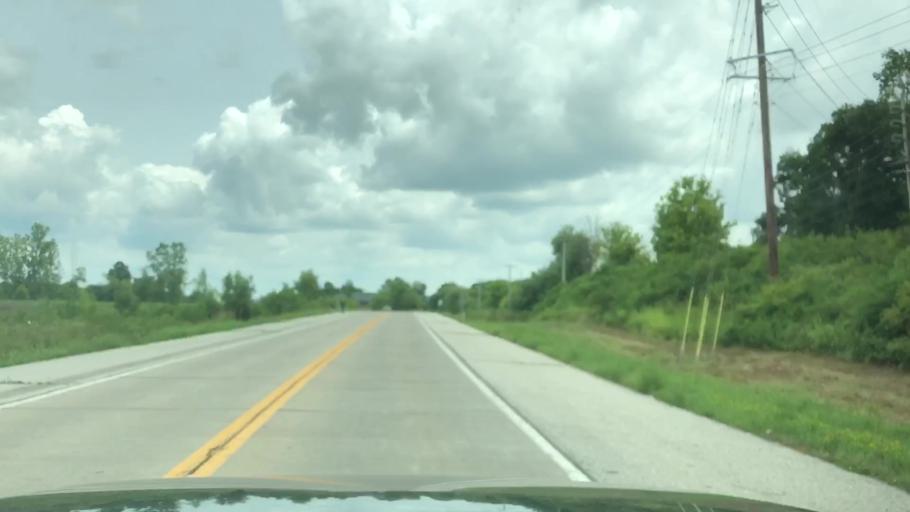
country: US
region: Missouri
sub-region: Saint Charles County
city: Saint Charles
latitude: 38.8161
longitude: -90.5200
